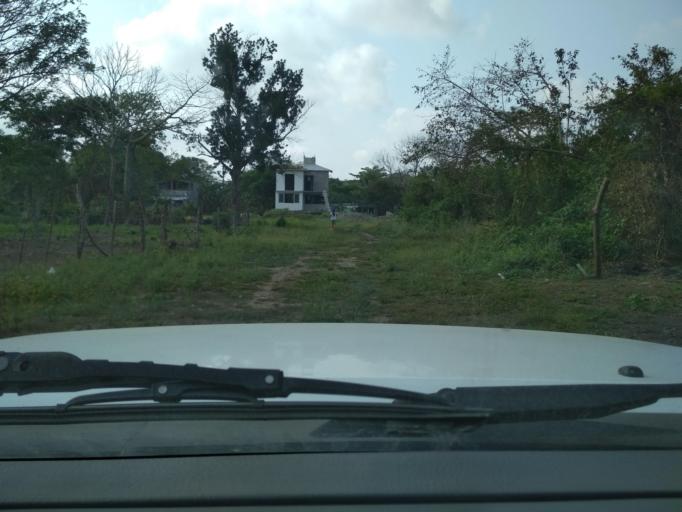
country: MX
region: Veracruz
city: El Tejar
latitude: 19.0847
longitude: -96.1661
